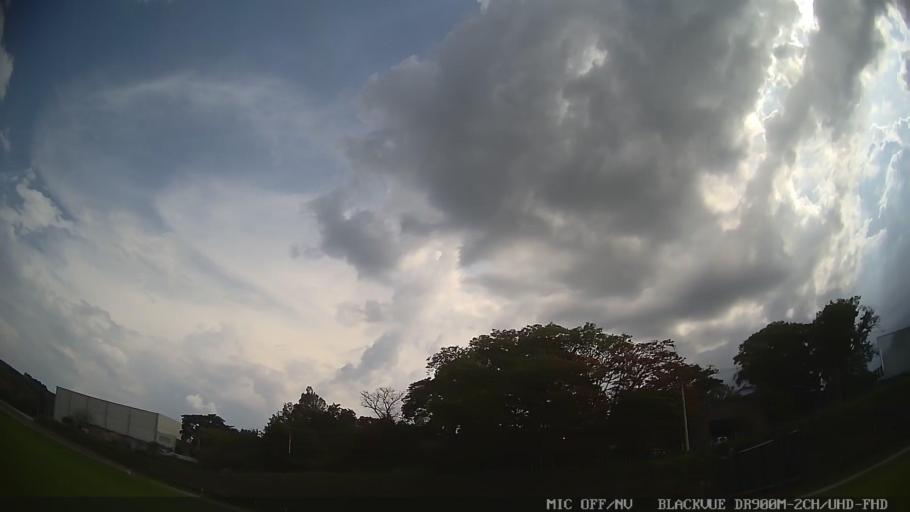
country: BR
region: Sao Paulo
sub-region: Itatiba
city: Itatiba
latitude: -23.0395
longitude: -46.8461
